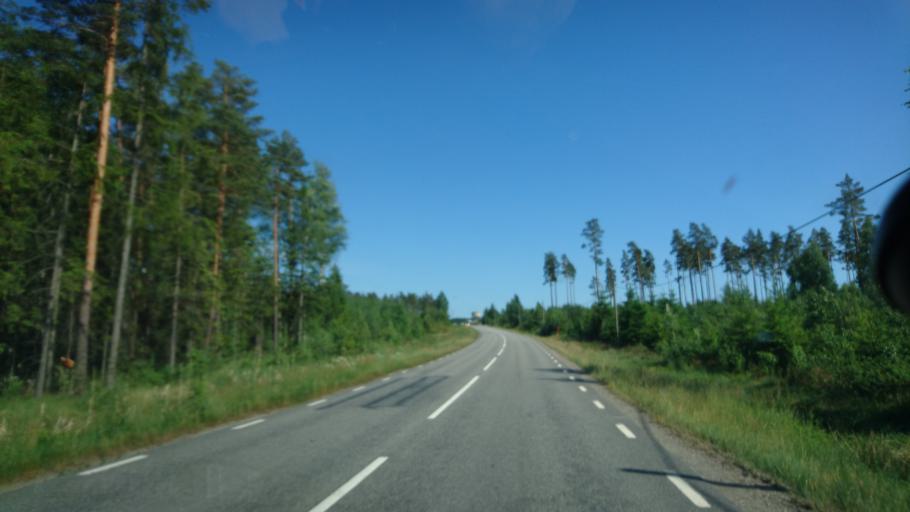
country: SE
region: Skane
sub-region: Osby Kommun
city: Lonsboda
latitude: 56.4131
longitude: 14.3015
